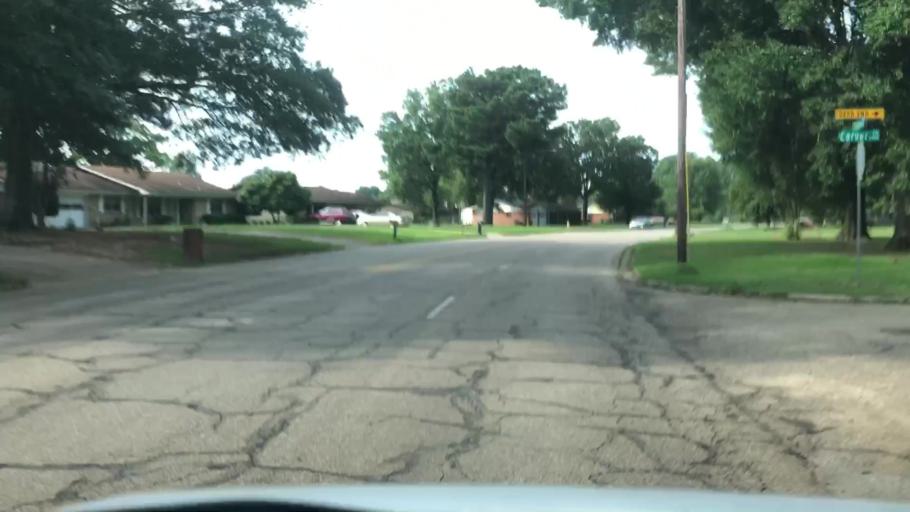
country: US
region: Texas
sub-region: Bowie County
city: Wake Village
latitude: 33.4049
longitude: -94.0791
